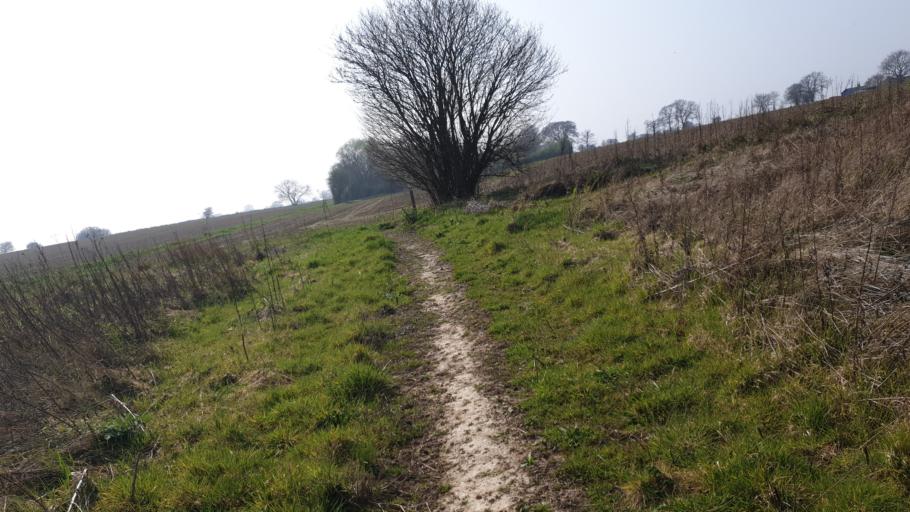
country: GB
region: England
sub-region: Essex
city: Mistley
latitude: 51.9310
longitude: 1.1664
